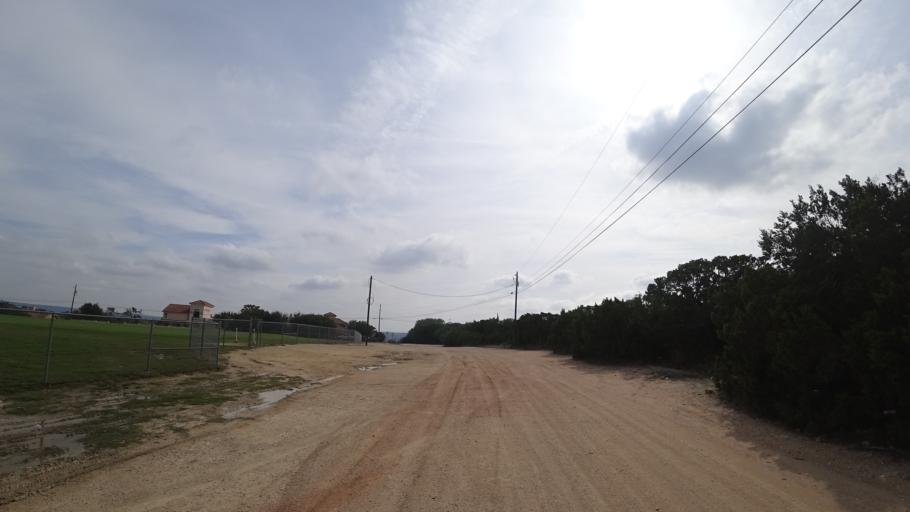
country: US
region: Texas
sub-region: Travis County
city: Hudson Bend
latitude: 30.3883
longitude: -97.9345
